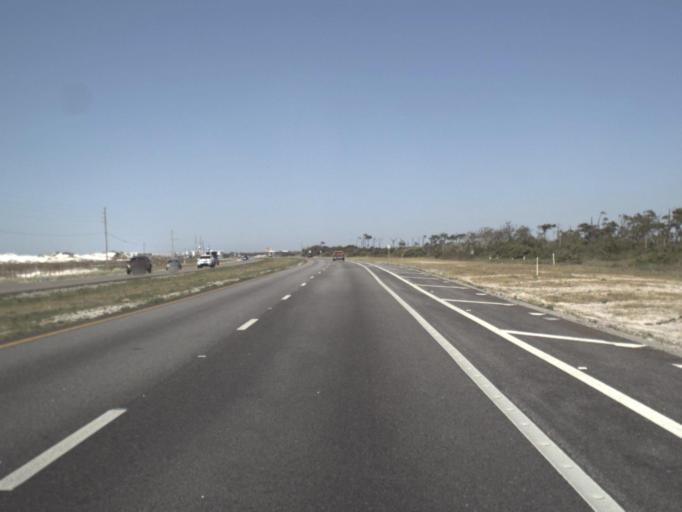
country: US
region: Florida
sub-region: Okaloosa County
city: Lake Lorraine
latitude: 30.3934
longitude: -86.5513
